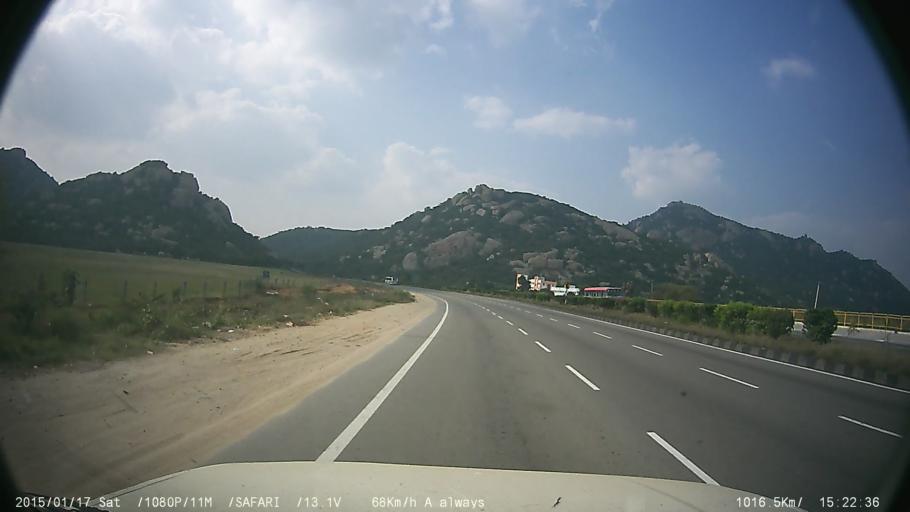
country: IN
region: Tamil Nadu
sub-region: Krishnagiri
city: Krishnagiri
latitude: 12.6036
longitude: 78.1212
